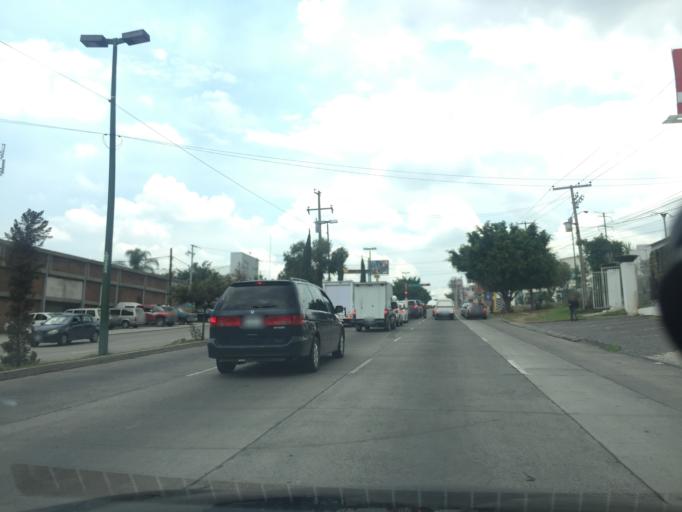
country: MX
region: Guanajuato
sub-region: Leon
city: La Ermita
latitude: 21.1472
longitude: -101.7077
